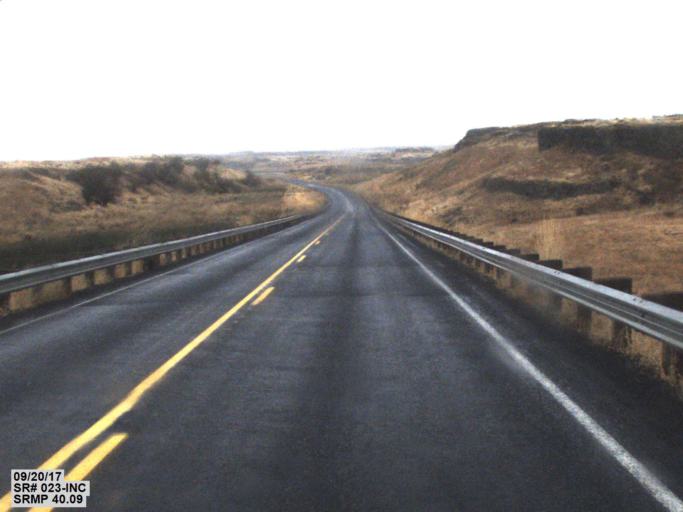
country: US
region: Washington
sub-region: Spokane County
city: Medical Lake
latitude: 47.2679
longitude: -117.9364
